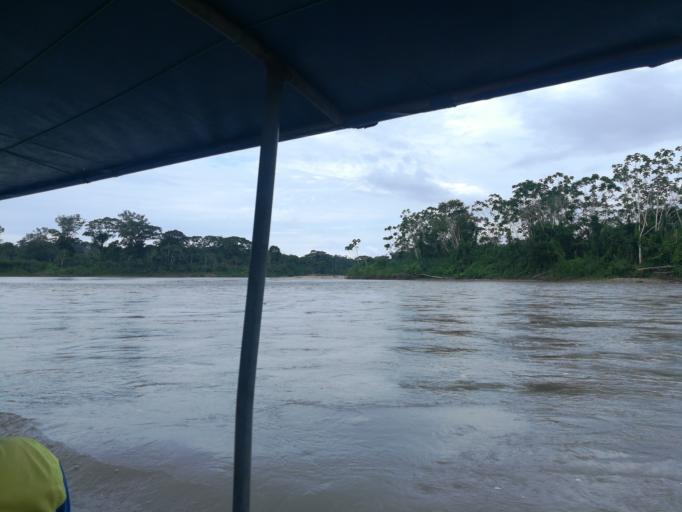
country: EC
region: Orellana
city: Boca Suno
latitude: -0.7560
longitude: -77.1539
